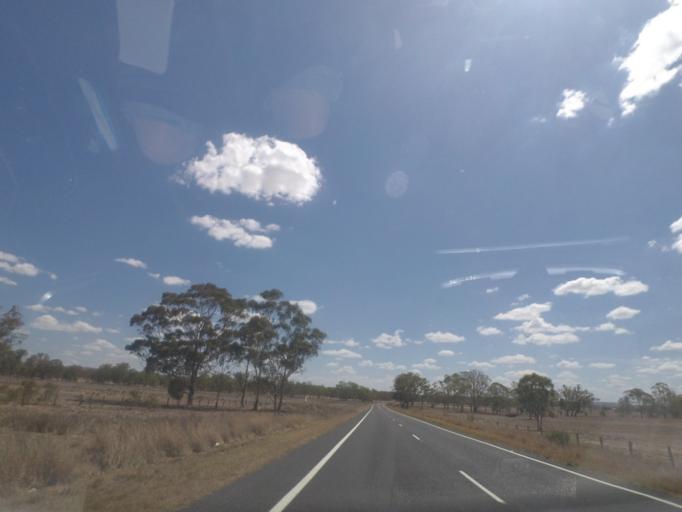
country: AU
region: Queensland
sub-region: Southern Downs
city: Warwick
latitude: -28.1816
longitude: 151.8201
